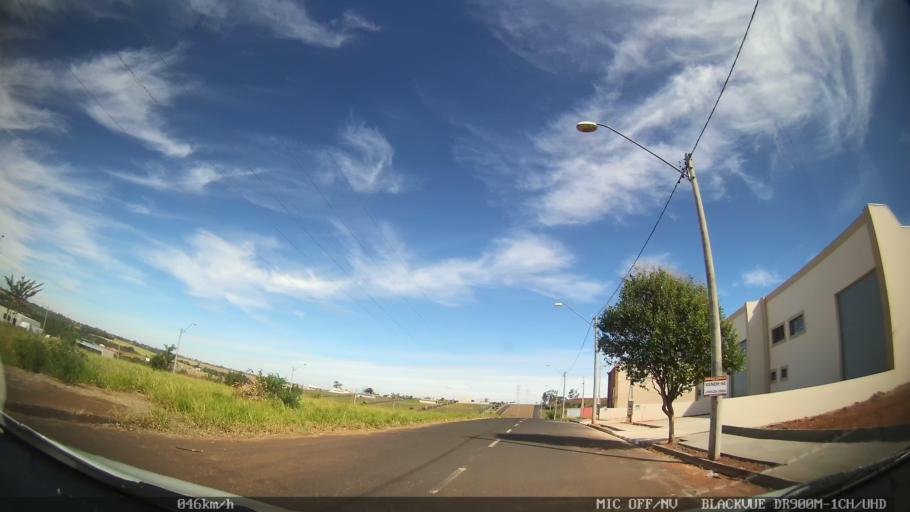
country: BR
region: Sao Paulo
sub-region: Sao Jose Do Rio Preto
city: Sao Jose do Rio Preto
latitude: -20.8464
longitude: -49.3725
